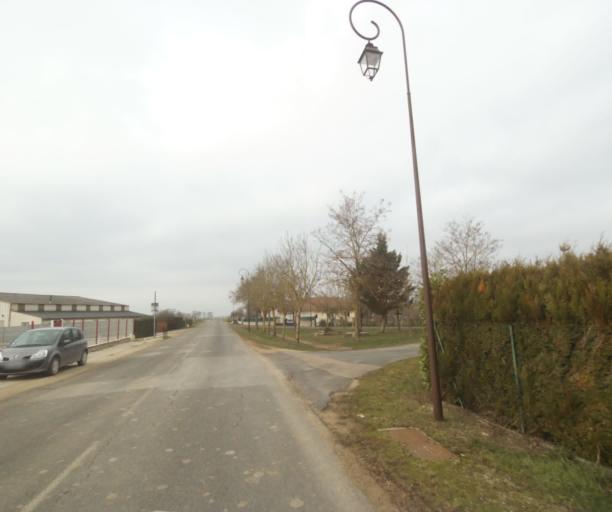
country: FR
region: Champagne-Ardenne
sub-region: Departement de la Haute-Marne
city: Villiers-en-Lieu
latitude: 48.6511
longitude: 4.8094
